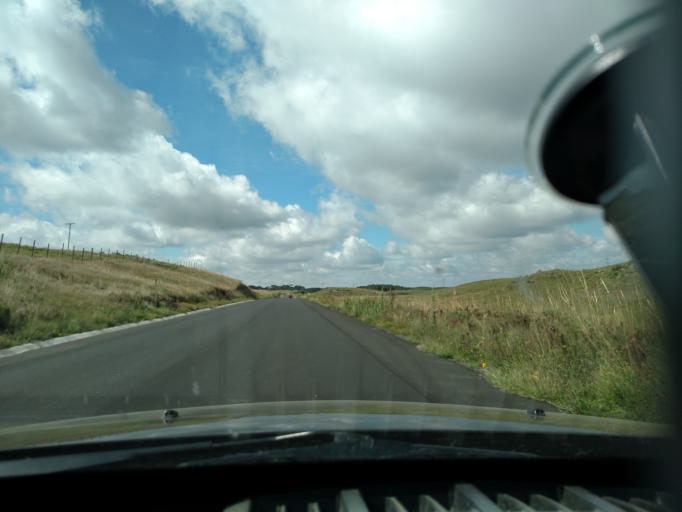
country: BR
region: Santa Catarina
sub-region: Lages
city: Lages
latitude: -28.0108
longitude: -50.0855
